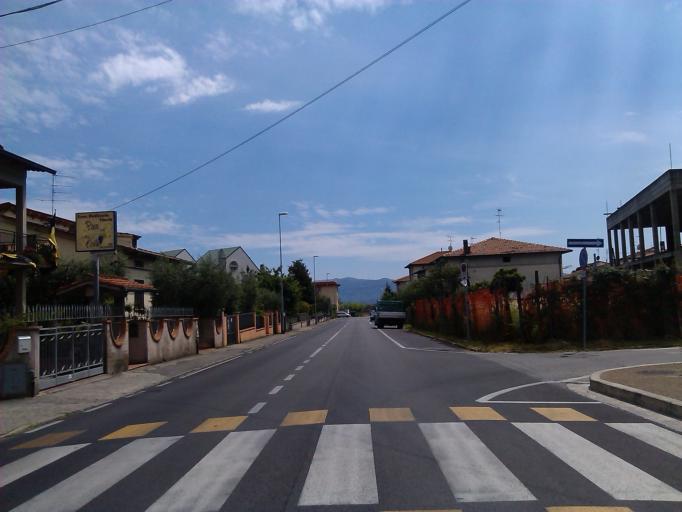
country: IT
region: Tuscany
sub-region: Provincia di Pistoia
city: Montale
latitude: 43.9339
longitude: 11.0252
